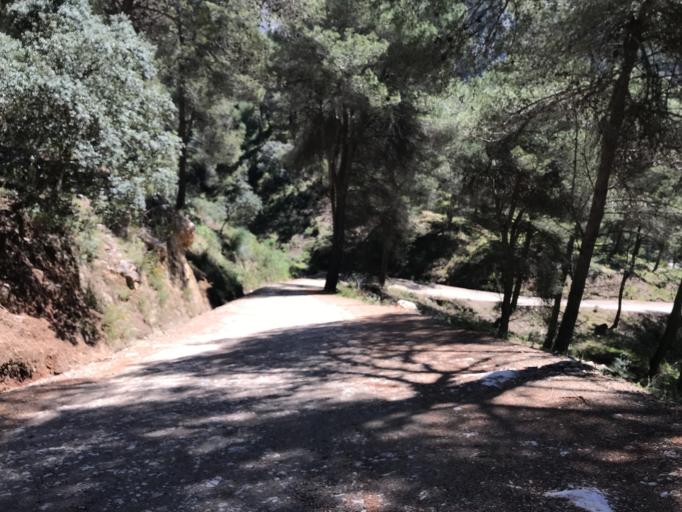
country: ES
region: Andalusia
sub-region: Provincia de Malaga
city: Alcaucin
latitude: 36.9172
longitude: -4.0926
